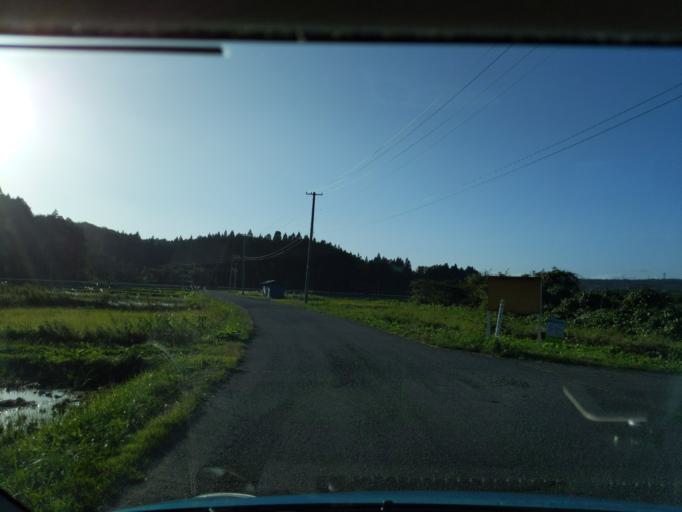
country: JP
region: Iwate
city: Ichinoseki
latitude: 38.9391
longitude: 141.0535
